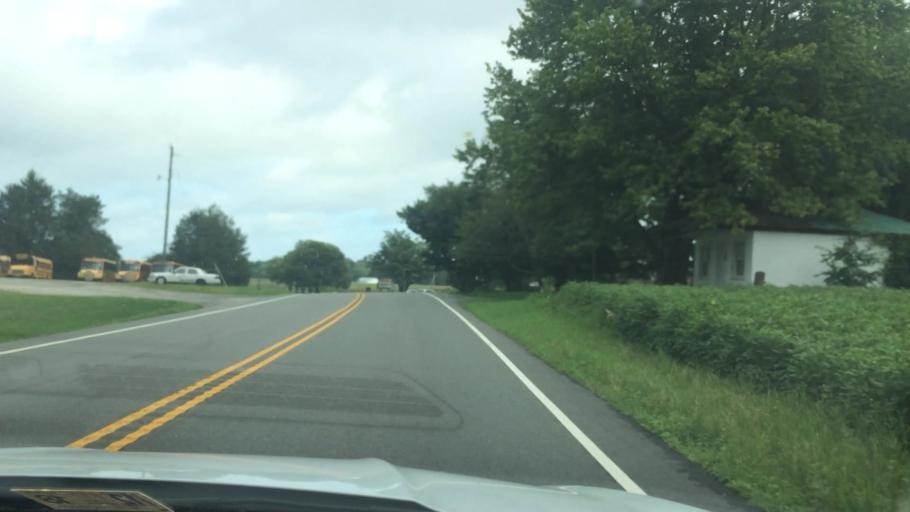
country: US
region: Virginia
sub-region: King William County
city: West Point
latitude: 37.6122
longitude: -76.7822
